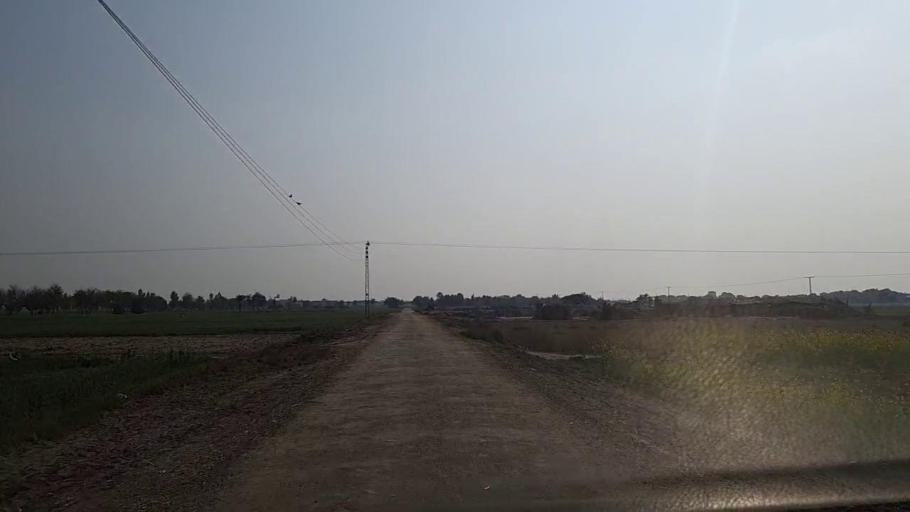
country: PK
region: Sindh
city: Daur
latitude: 26.4046
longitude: 68.4201
